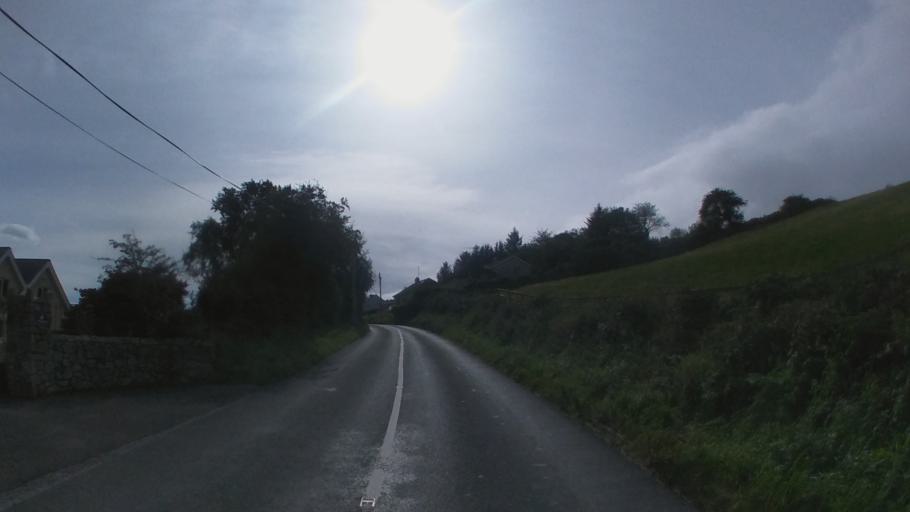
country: IE
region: Leinster
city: Sandyford
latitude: 53.2426
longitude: -6.2224
